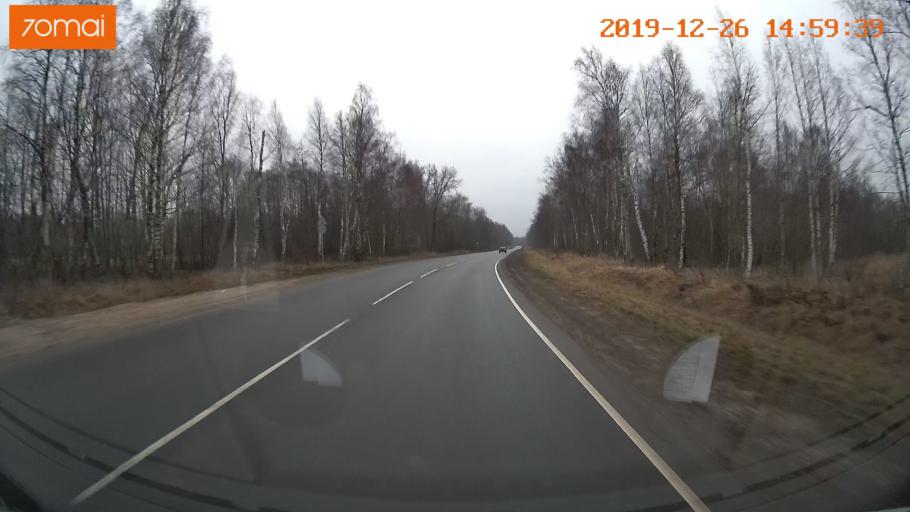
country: RU
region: Jaroslavl
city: Rybinsk
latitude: 58.2563
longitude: 38.8489
